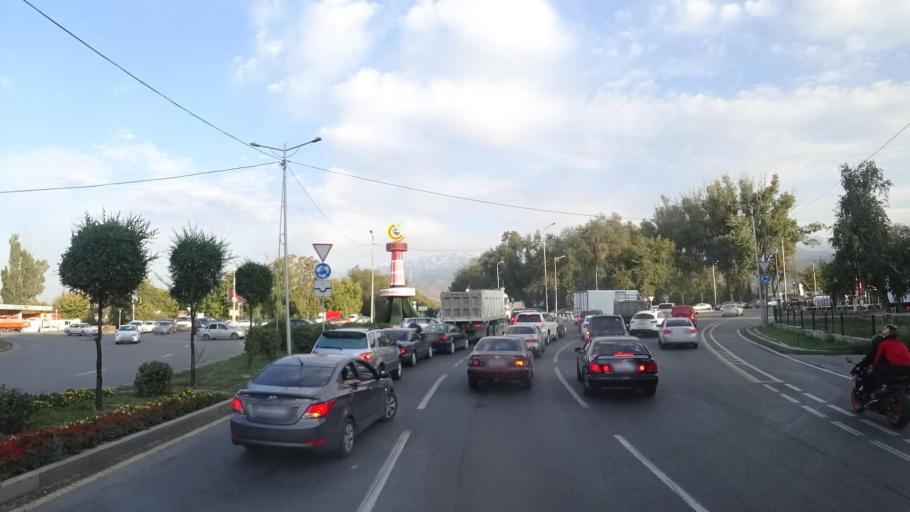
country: KZ
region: Almaty Oblysy
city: Pervomayskiy
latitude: 43.3202
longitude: 77.0249
